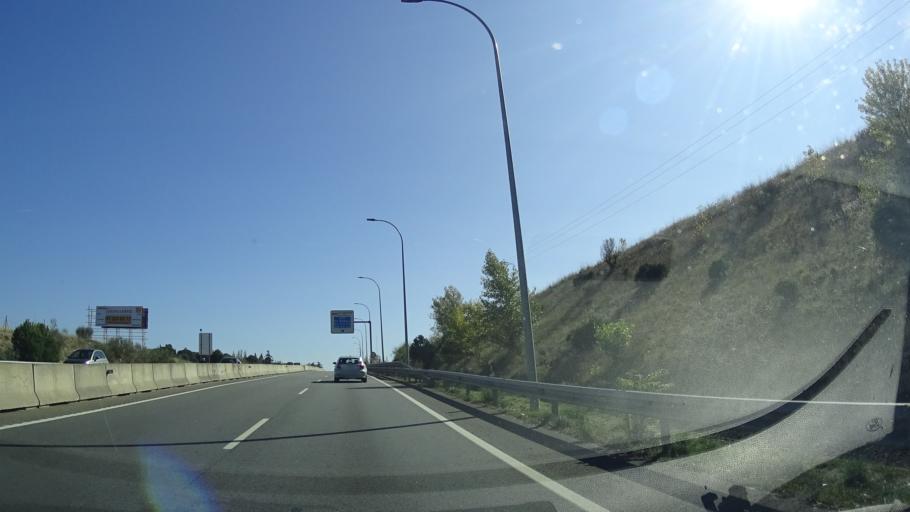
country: ES
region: Madrid
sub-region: Provincia de Madrid
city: Las Rozas de Madrid
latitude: 40.5027
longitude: -3.9048
